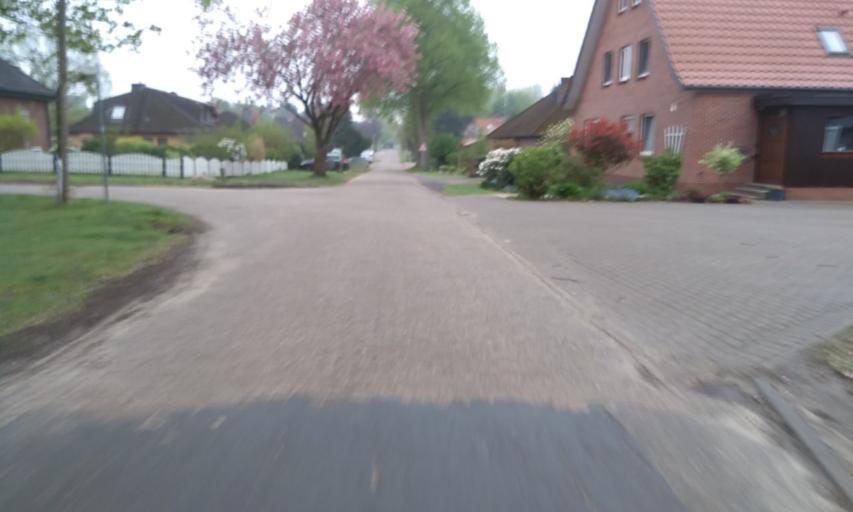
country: DE
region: Lower Saxony
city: Bliedersdorf
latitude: 53.4552
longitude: 9.5612
